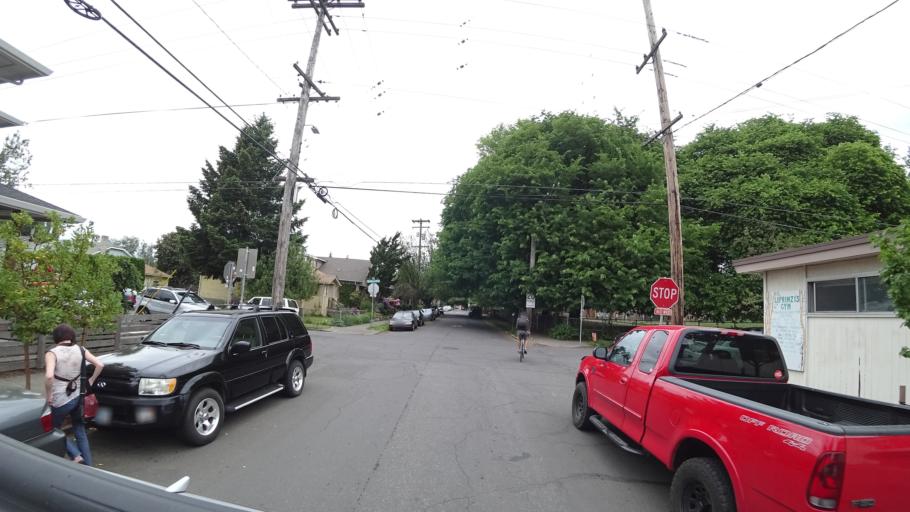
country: US
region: Oregon
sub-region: Multnomah County
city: Portland
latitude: 45.5053
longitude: -122.6203
